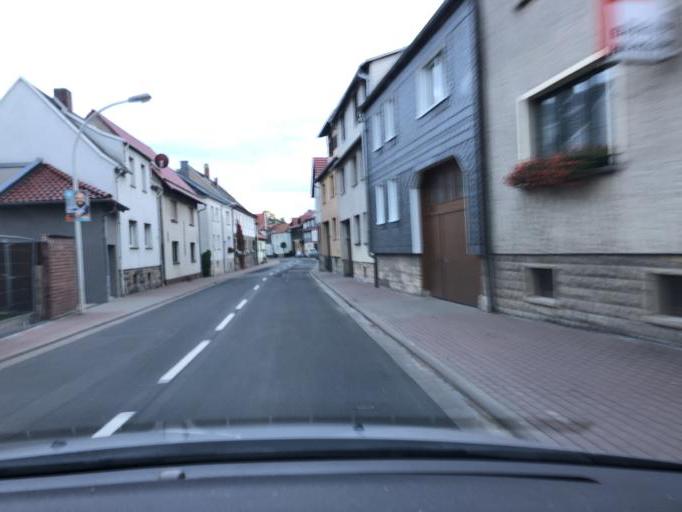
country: DE
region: Thuringia
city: Buttstedt
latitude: 51.2244
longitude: 10.3027
